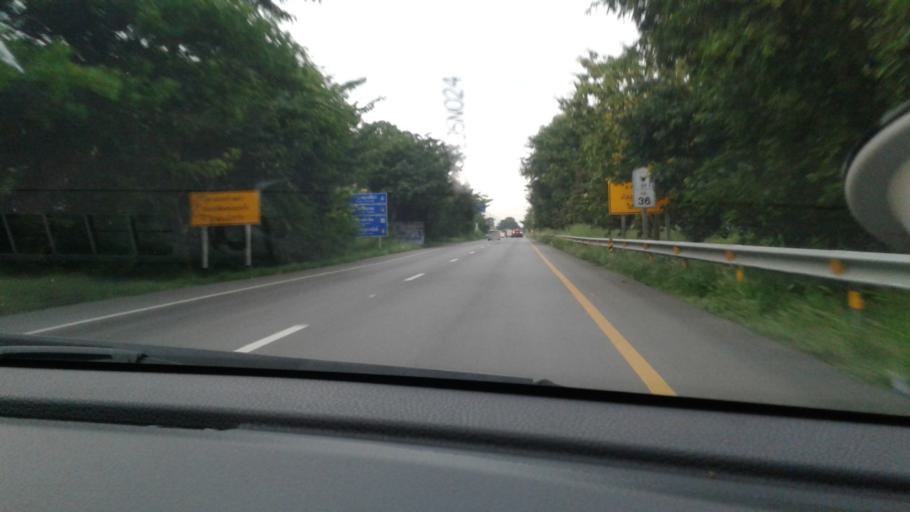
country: TH
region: Prachuap Khiri Khan
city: Hua Hin
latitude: 12.5126
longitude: 99.8836
